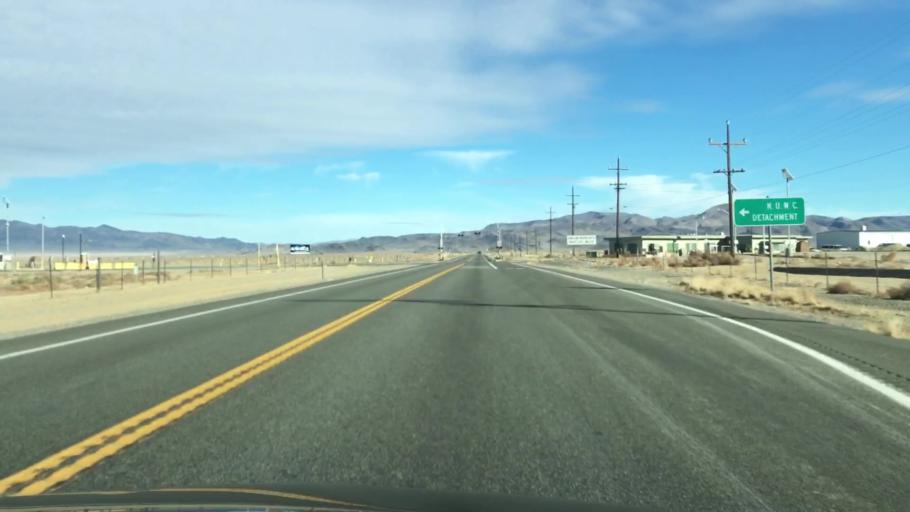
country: US
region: Nevada
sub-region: Mineral County
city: Hawthorne
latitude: 38.5245
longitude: -118.6001
